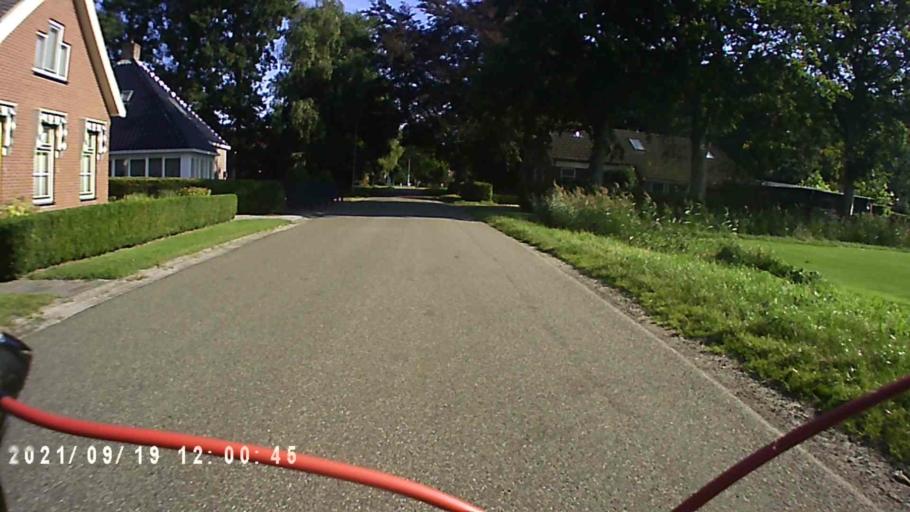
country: NL
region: Groningen
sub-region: Gemeente Slochteren
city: Slochteren
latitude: 53.2270
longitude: 6.8013
